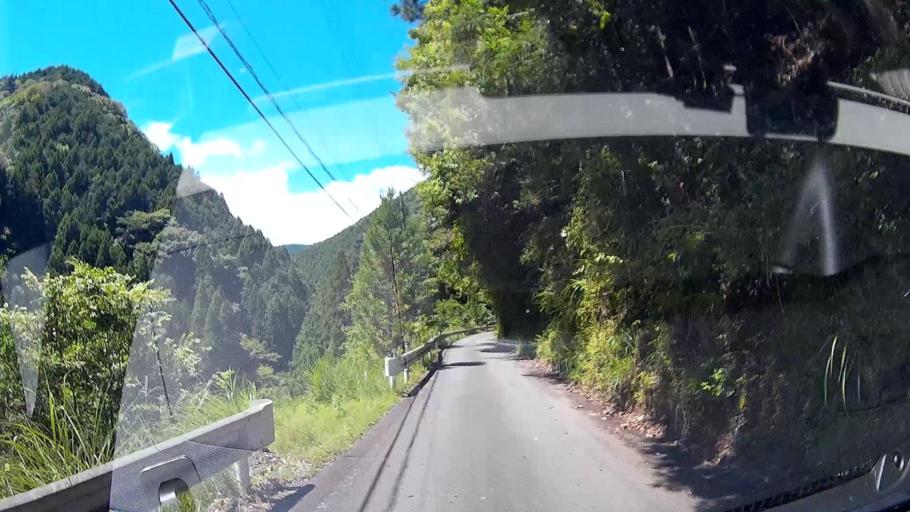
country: JP
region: Shizuoka
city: Shizuoka-shi
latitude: 35.1767
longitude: 138.2858
